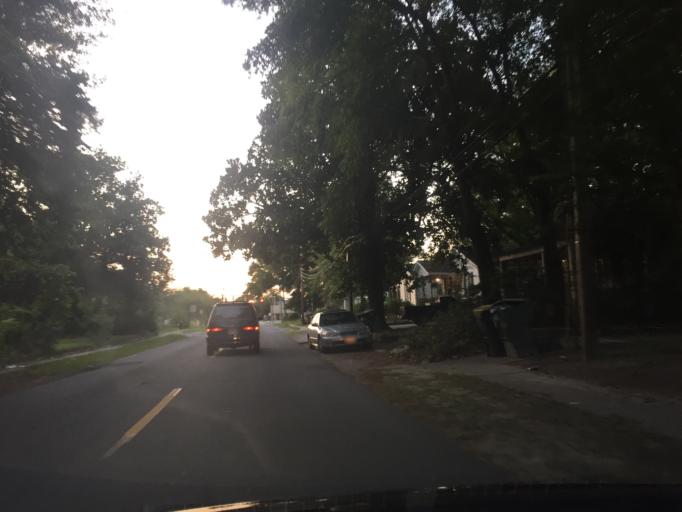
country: US
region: Georgia
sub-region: Chatham County
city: Thunderbolt
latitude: 32.0581
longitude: -81.0632
